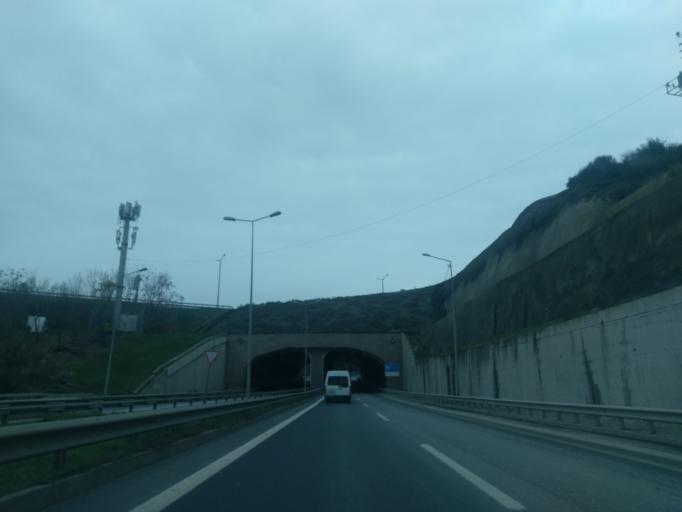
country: TR
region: Istanbul
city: Sisli
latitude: 41.0958
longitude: 28.9536
